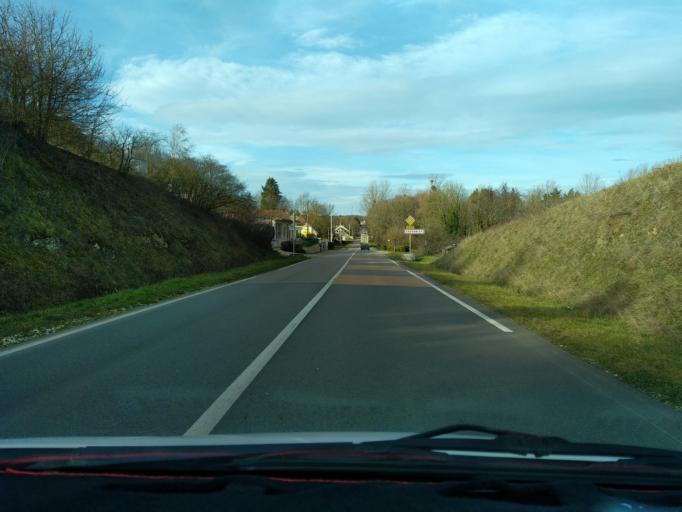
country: FR
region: Franche-Comte
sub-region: Departement de la Haute-Saone
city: Gray
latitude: 47.3877
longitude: 5.6551
